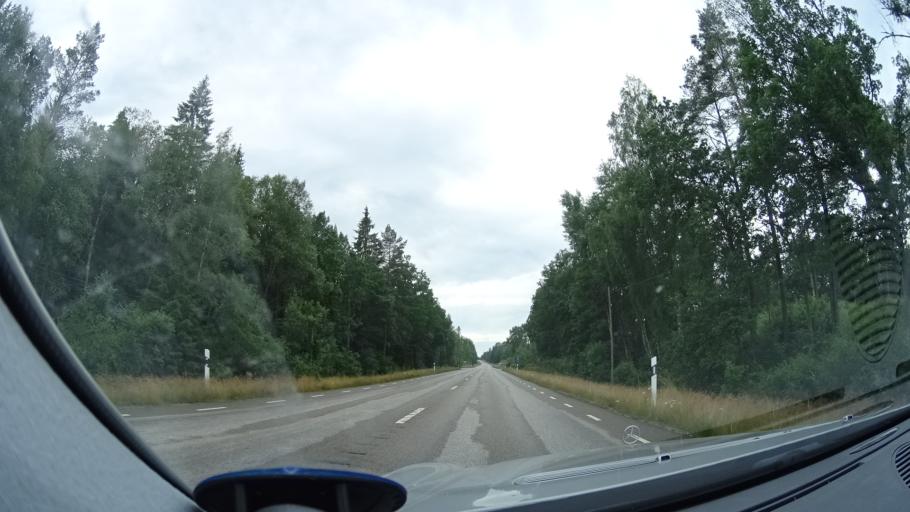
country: SE
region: Kronoberg
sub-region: Tingsryds Kommun
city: Tingsryd
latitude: 56.4429
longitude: 14.9807
